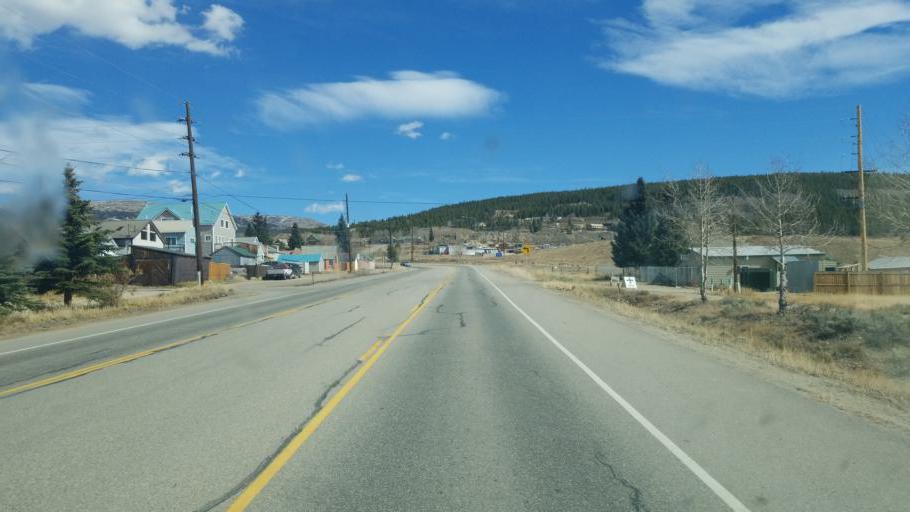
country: US
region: Colorado
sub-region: Lake County
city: Leadville
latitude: 39.2426
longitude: -106.2928
